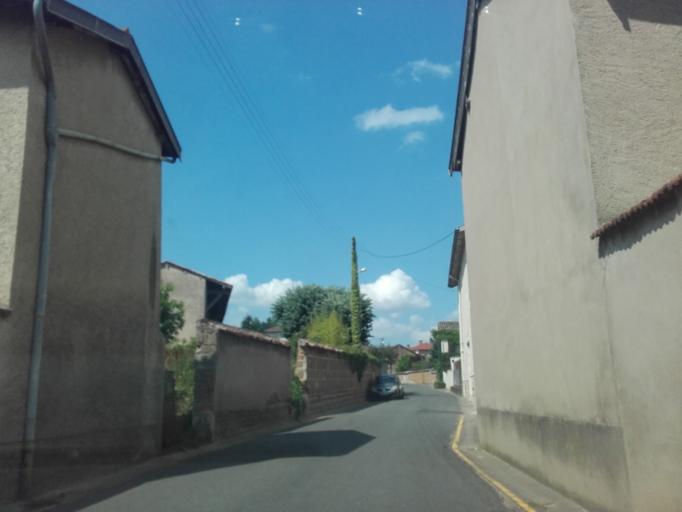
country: FR
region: Bourgogne
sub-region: Departement de Saone-et-Loire
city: La Chapelle-de-Guinchay
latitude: 46.1992
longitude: 4.7690
